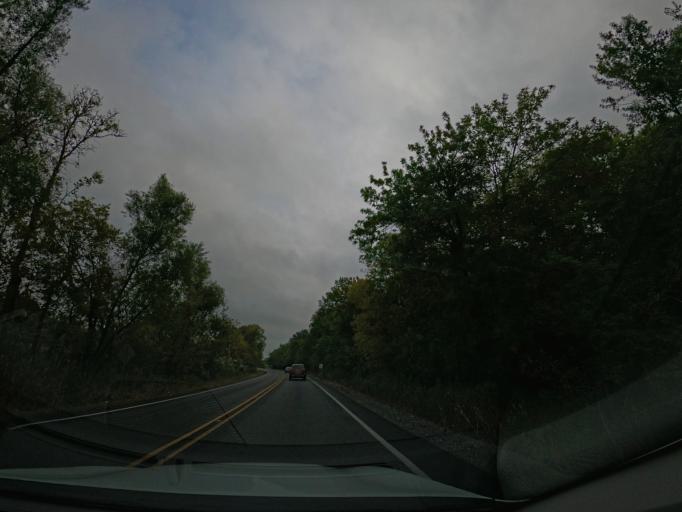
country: US
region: Louisiana
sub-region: Terrebonne Parish
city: Presquille
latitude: 29.4998
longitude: -90.6790
